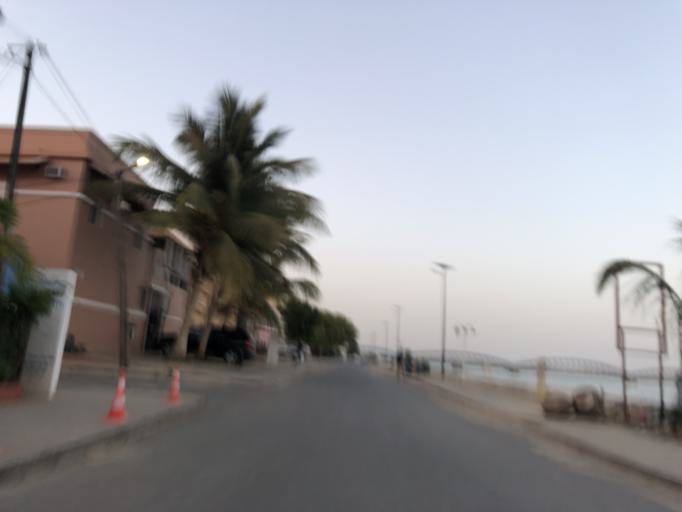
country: SN
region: Saint-Louis
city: Saint-Louis
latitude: 16.0227
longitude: -16.5040
